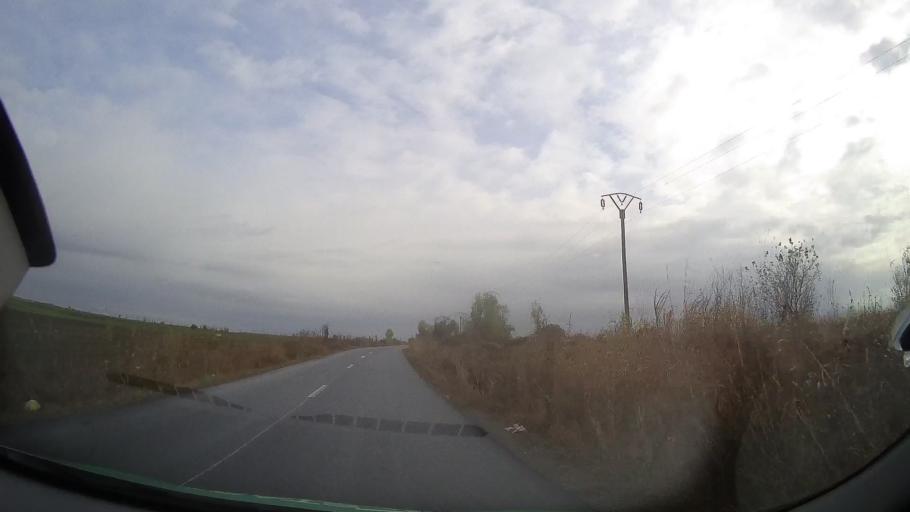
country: RO
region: Ialomita
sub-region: Comuna Maia
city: Maia
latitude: 44.7517
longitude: 26.3886
